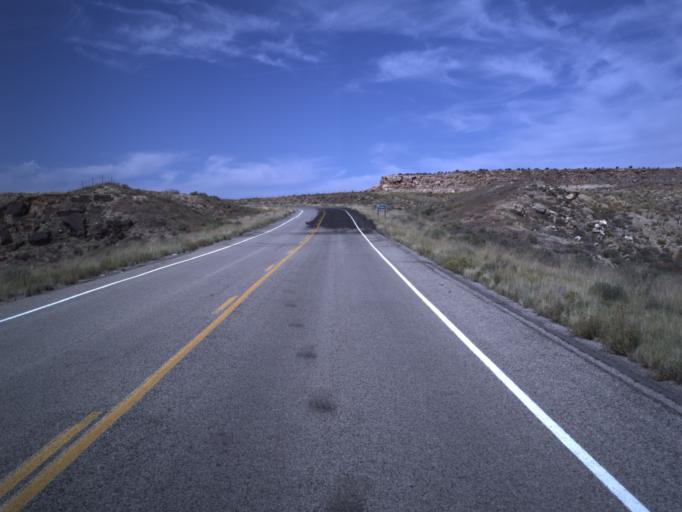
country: US
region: Colorado
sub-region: Montezuma County
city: Towaoc
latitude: 37.1535
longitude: -109.0495
